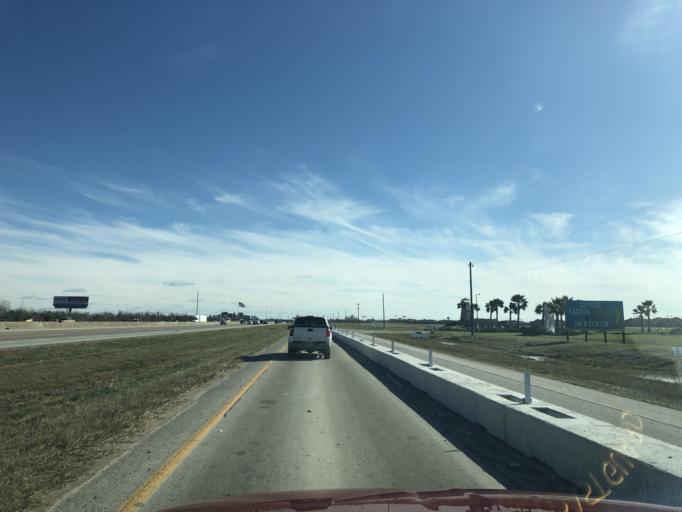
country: US
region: Texas
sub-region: Galveston County
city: Dickinson
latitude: 29.4180
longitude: -95.0485
